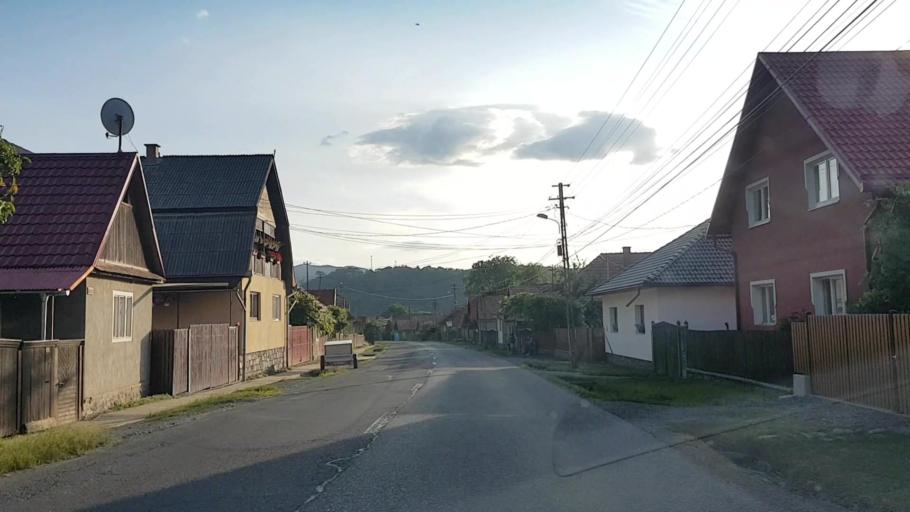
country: RO
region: Harghita
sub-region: Comuna Praid
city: Praid
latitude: 46.5602
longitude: 25.1397
